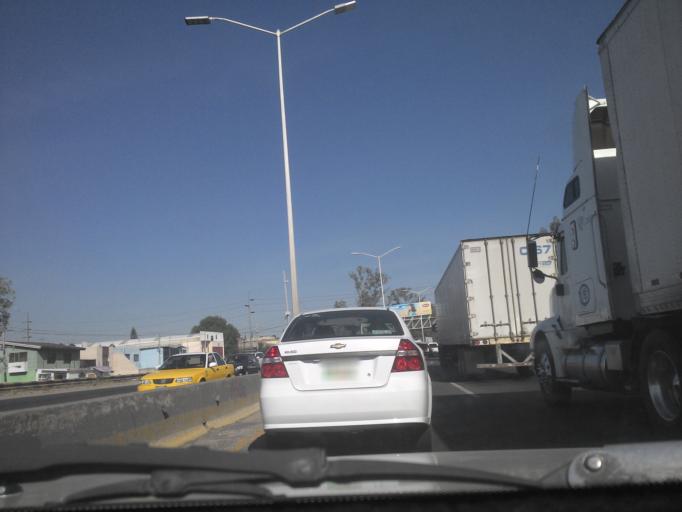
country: MX
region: Jalisco
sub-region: Tlajomulco de Zuniga
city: La Tijera
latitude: 20.6121
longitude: -103.4222
